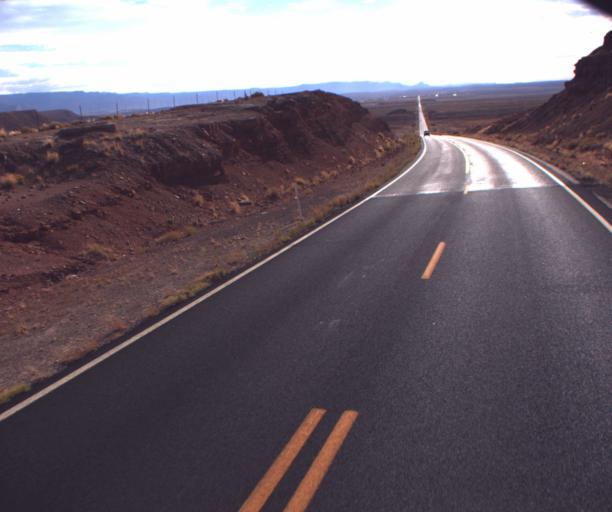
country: US
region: Arizona
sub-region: Apache County
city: Many Farms
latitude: 36.5447
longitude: -109.5294
